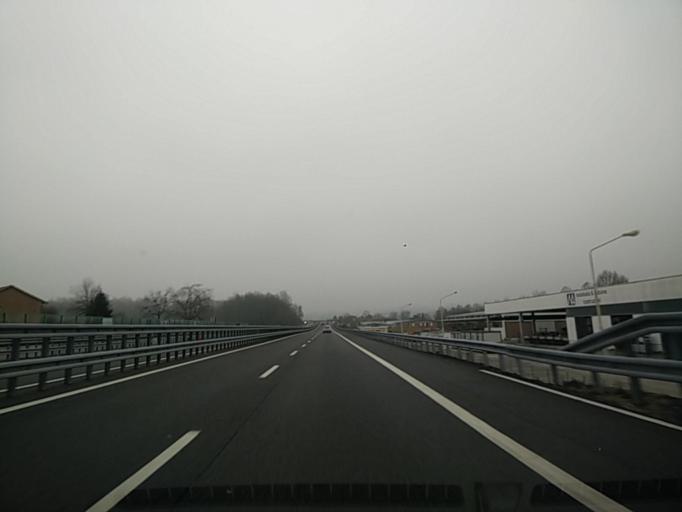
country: IT
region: Piedmont
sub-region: Provincia di Asti
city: Cantarana
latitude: 44.9072
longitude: 8.0522
